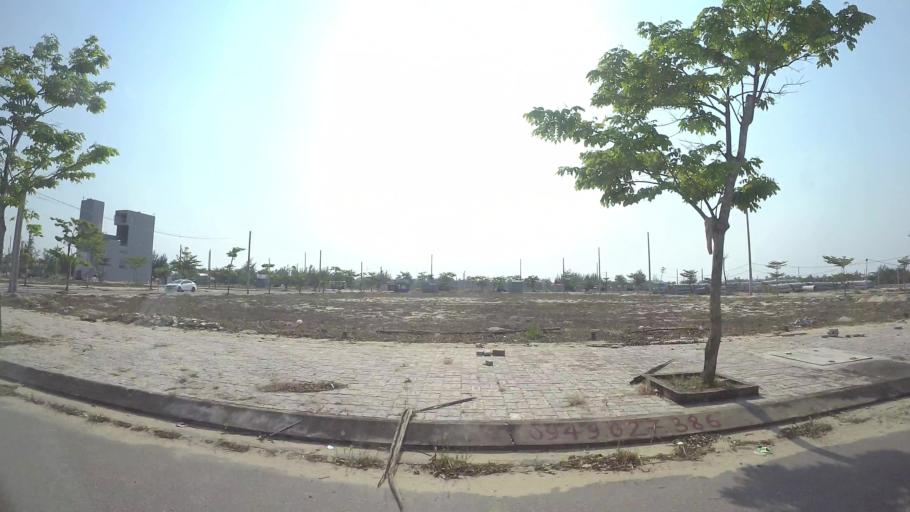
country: VN
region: Da Nang
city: Ngu Hanh Son
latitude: 15.9544
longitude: 108.2755
